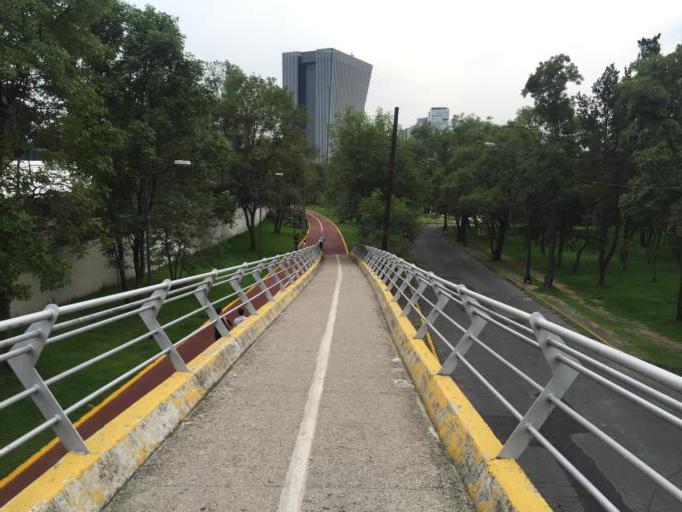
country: MX
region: Mexico City
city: Polanco
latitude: 19.4210
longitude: -99.1990
